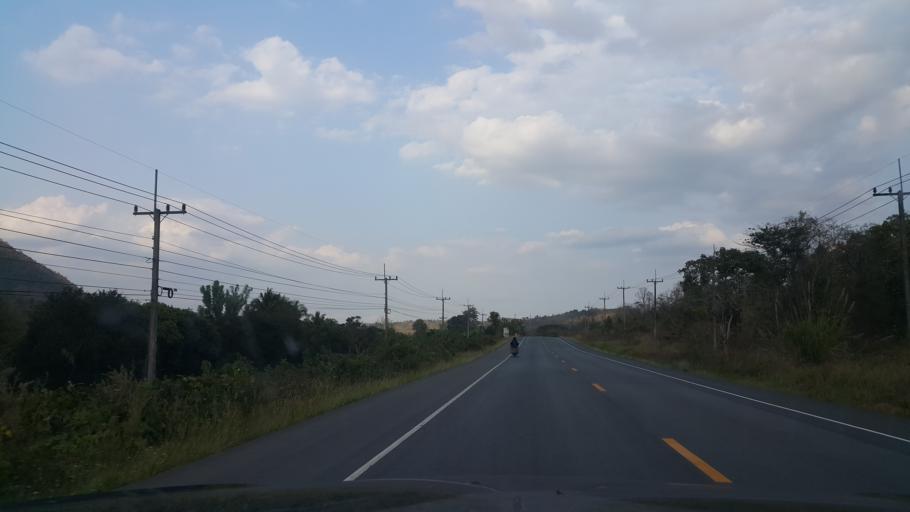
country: TH
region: Loei
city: Dan Sai
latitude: 17.3282
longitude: 101.2214
